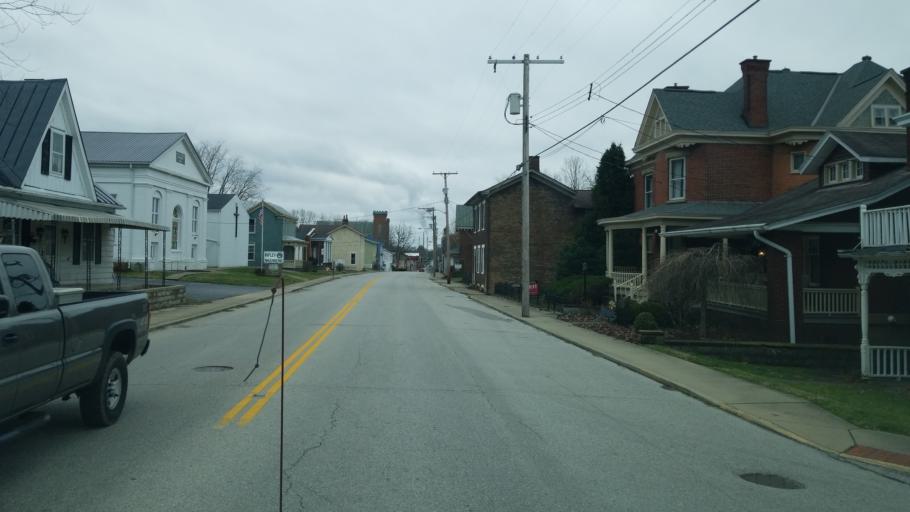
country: US
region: Ohio
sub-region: Brown County
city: Ripley
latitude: 38.7497
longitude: -83.8480
